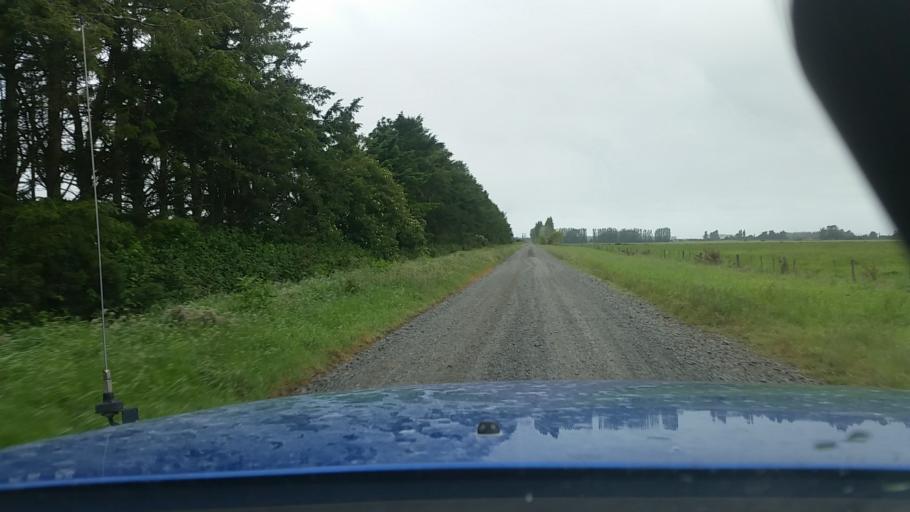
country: NZ
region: Canterbury
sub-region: Ashburton District
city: Tinwald
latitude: -44.0014
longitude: 171.6613
